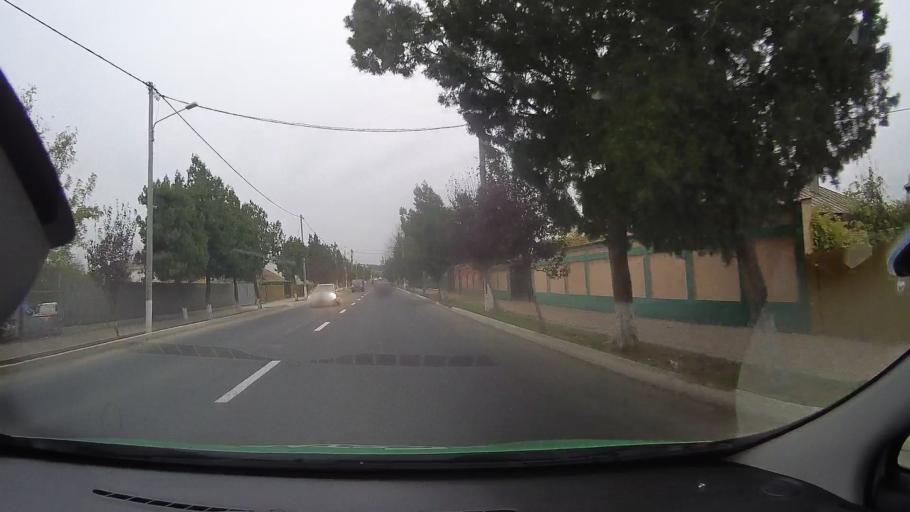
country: RO
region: Constanta
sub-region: Oras Harsova
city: Harsova
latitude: 44.6885
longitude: 27.9489
